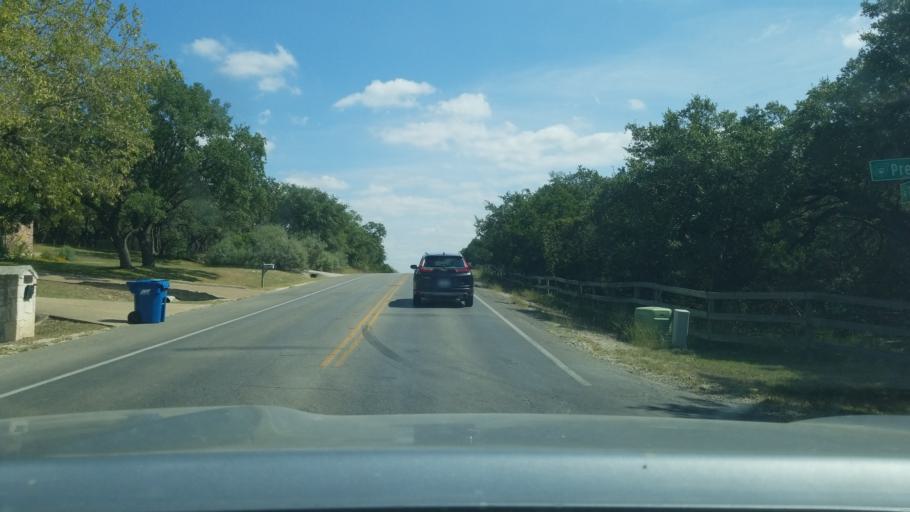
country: US
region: Texas
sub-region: Bexar County
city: Fair Oaks Ranch
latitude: 29.7311
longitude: -98.6297
